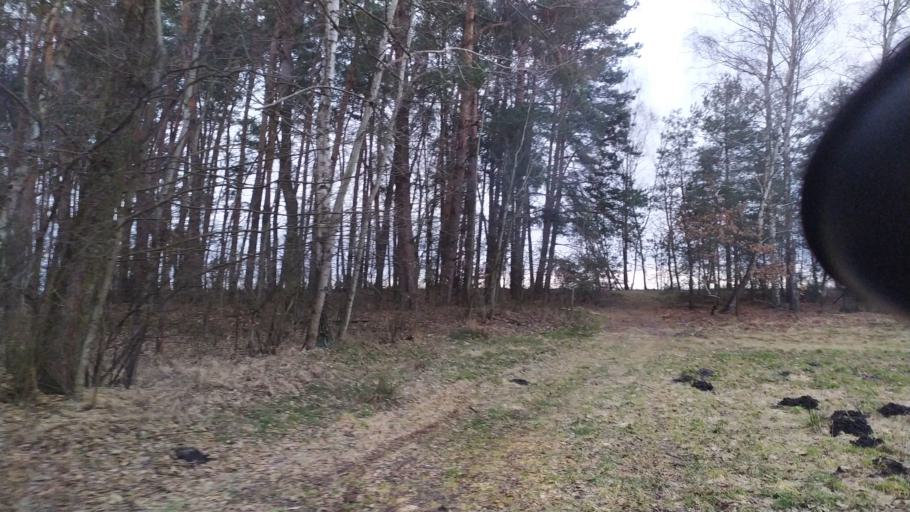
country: PL
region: Lublin Voivodeship
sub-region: Powiat lubartowski
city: Abramow
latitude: 51.4293
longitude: 22.2924
